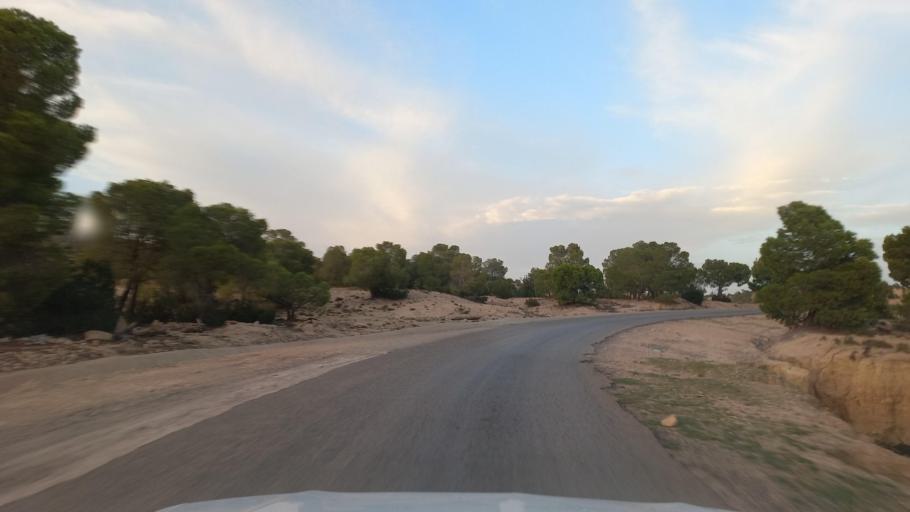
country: TN
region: Al Qasrayn
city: Sbiba
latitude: 35.4100
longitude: 8.9517
